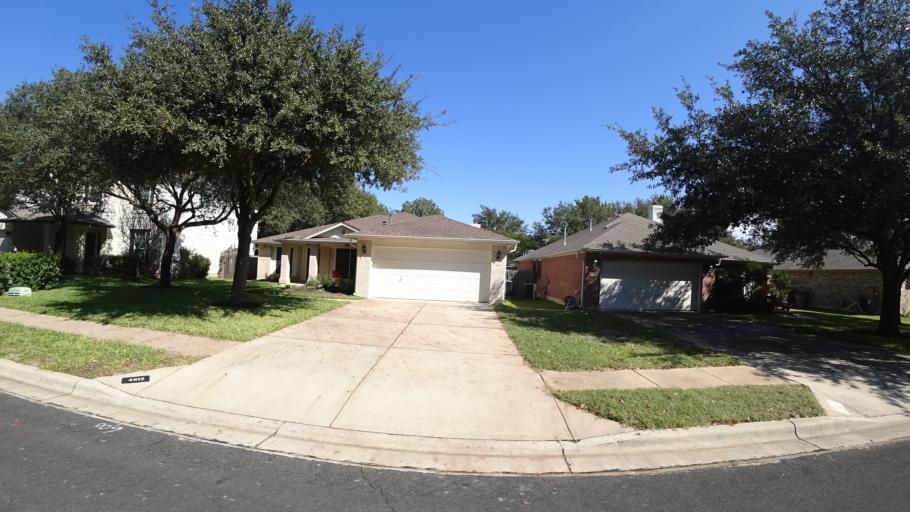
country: US
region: Texas
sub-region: Travis County
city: Shady Hollow
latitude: 30.1947
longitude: -97.8620
